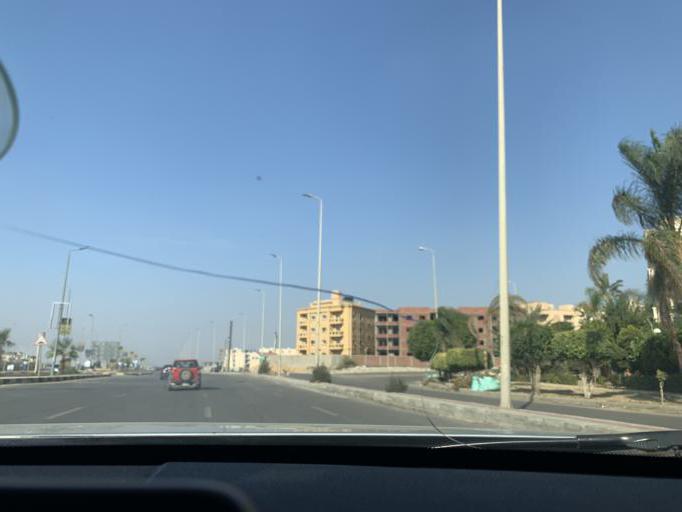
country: EG
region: Muhafazat al Qalyubiyah
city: Al Khankah
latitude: 30.0156
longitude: 31.4750
